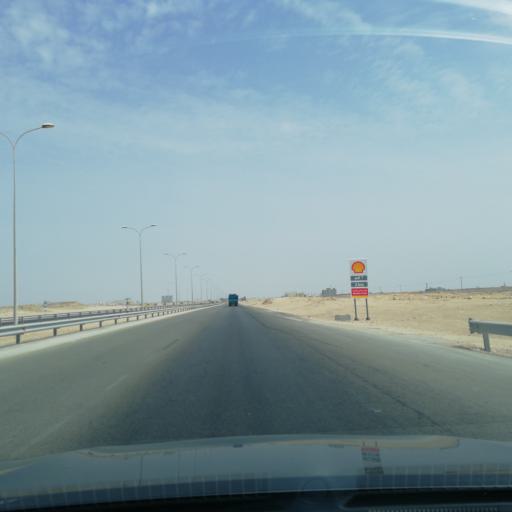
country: OM
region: Zufar
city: Salalah
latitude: 17.5952
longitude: 54.0386
